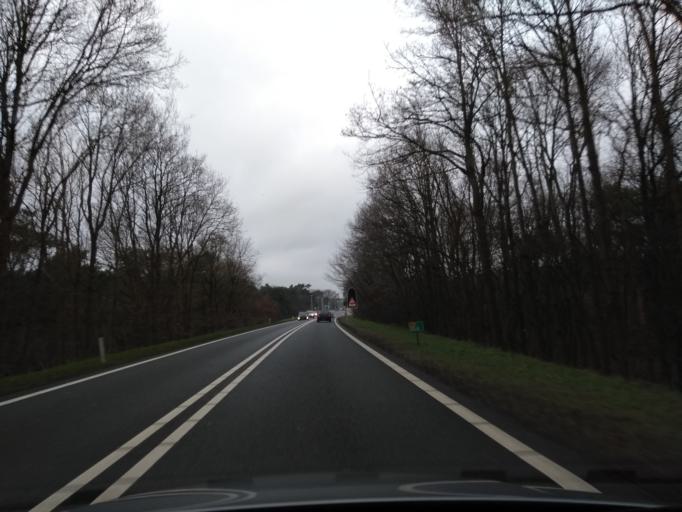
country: NL
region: Overijssel
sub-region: Gemeente Twenterand
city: Vroomshoop
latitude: 52.5070
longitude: 6.5658
